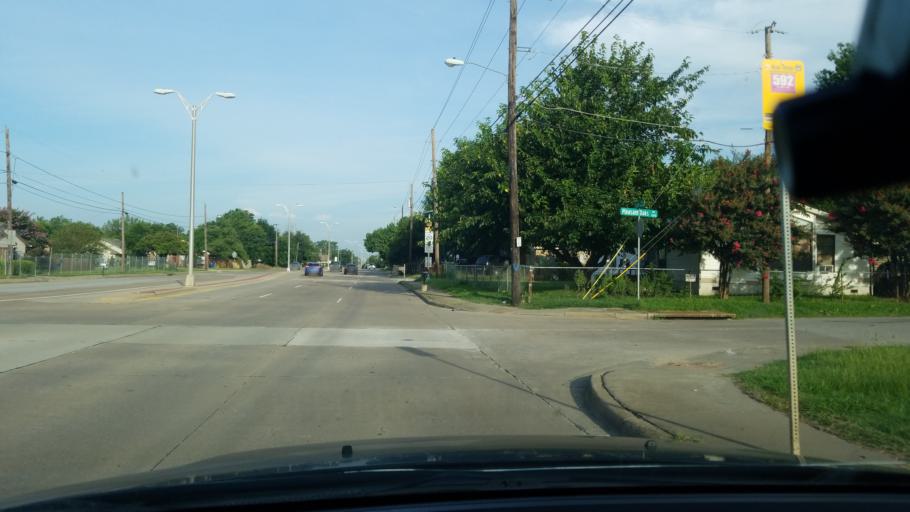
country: US
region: Texas
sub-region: Dallas County
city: Balch Springs
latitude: 32.7195
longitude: -96.6414
